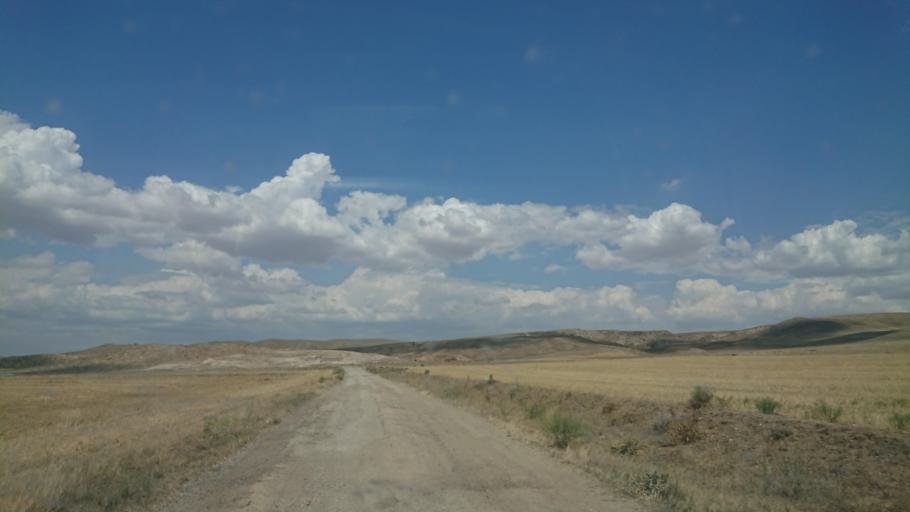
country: TR
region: Aksaray
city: Sariyahsi
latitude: 38.9922
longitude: 33.9120
